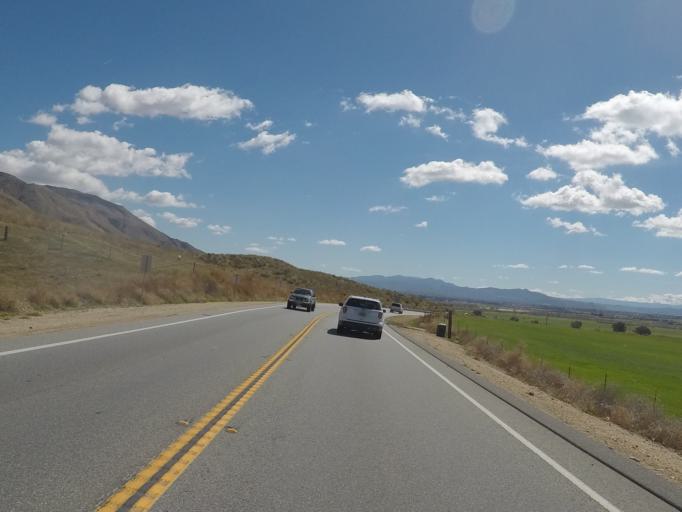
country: US
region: California
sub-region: Riverside County
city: Beaumont
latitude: 33.8514
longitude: -117.0129
